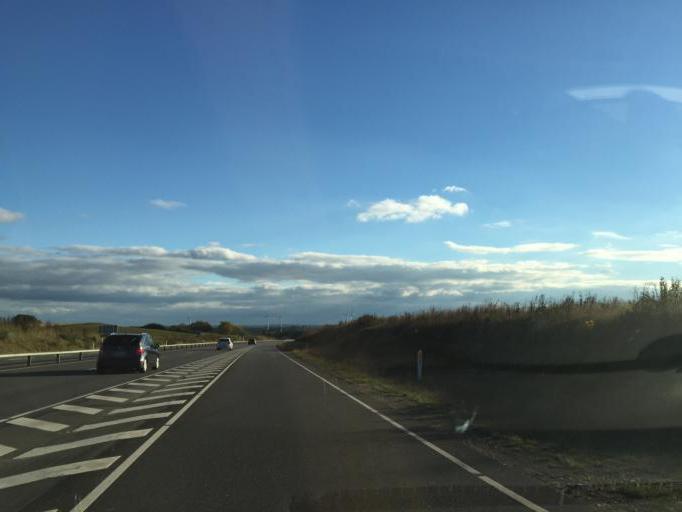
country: DK
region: Zealand
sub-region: Odsherred Kommune
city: Asnaes
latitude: 55.7900
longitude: 11.5831
